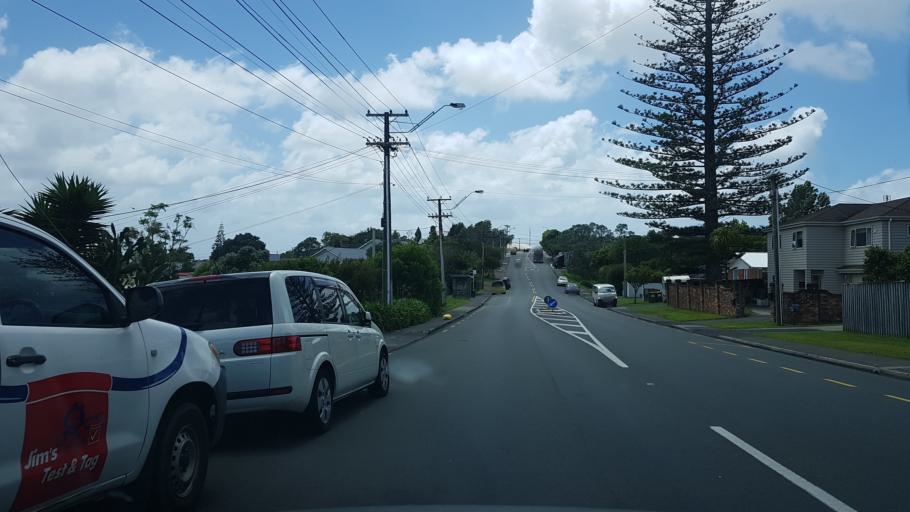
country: NZ
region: Auckland
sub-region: Auckland
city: North Shore
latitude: -36.8085
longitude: 174.7024
